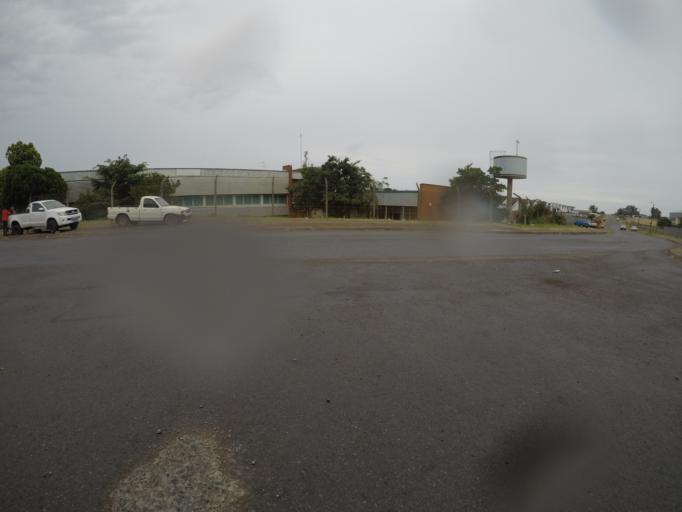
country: ZA
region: Eastern Cape
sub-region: Buffalo City Metropolitan Municipality
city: East London
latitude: -32.9725
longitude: 27.8231
